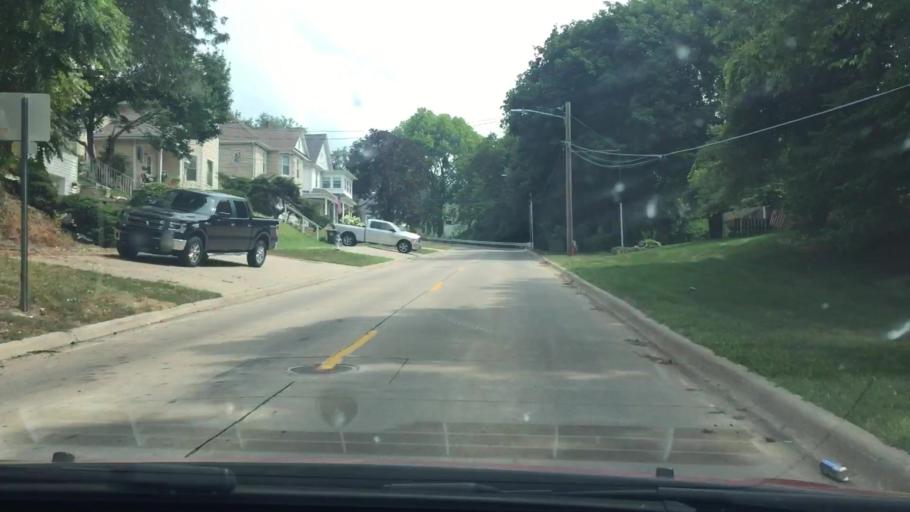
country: US
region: Iowa
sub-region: Muscatine County
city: Muscatine
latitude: 41.4170
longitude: -91.0569
